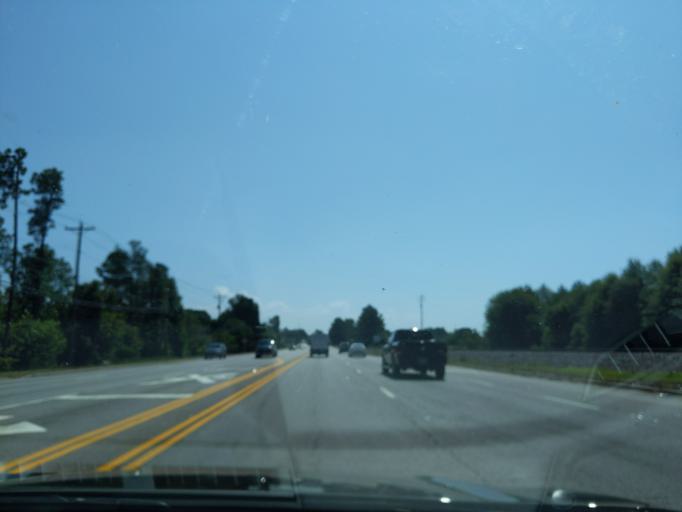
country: US
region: South Carolina
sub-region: Lexington County
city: Oak Grove
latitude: 33.9750
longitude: -81.1708
